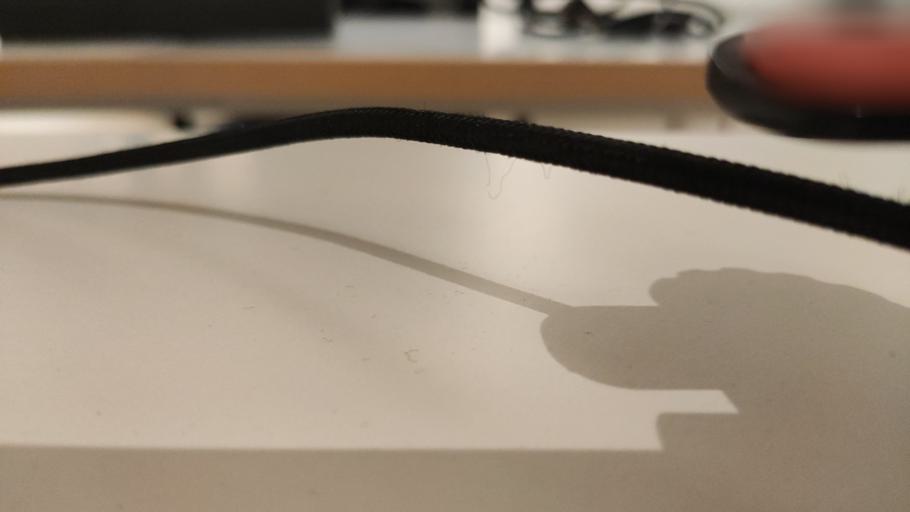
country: RU
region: Moskovskaya
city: Dorokhovo
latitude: 55.4867
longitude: 36.3561
